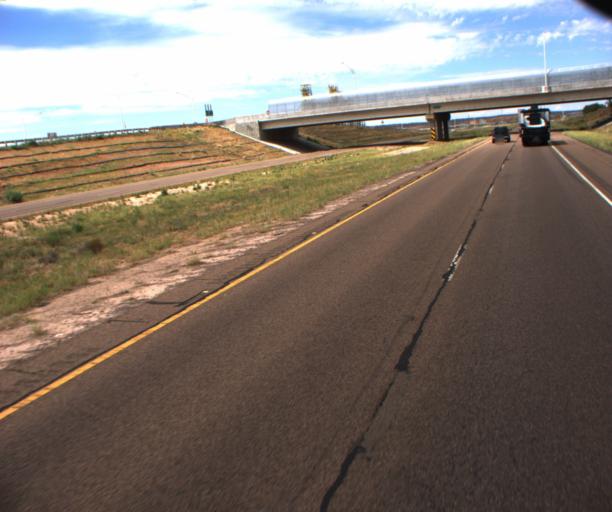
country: US
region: Arizona
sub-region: Apache County
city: Houck
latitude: 35.2165
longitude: -109.3322
